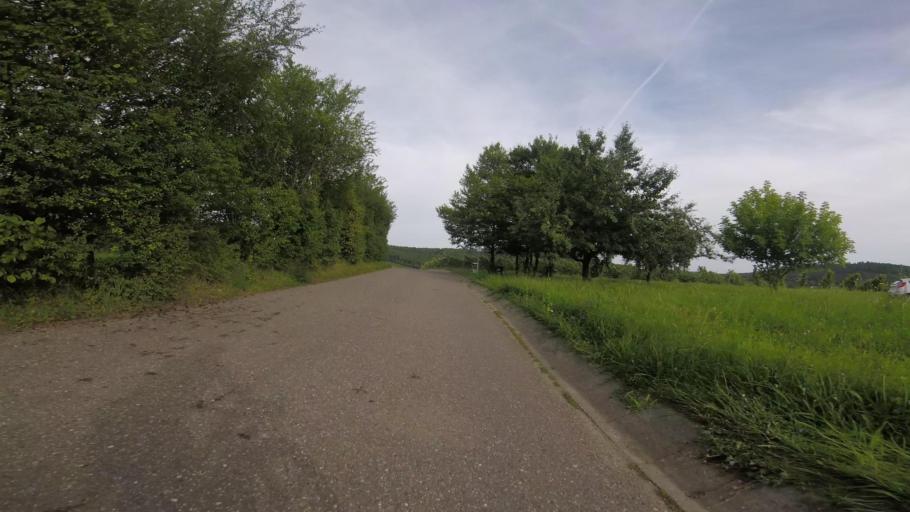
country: DE
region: Baden-Wuerttemberg
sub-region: Regierungsbezirk Stuttgart
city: Beilstein
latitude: 49.0634
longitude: 9.3148
